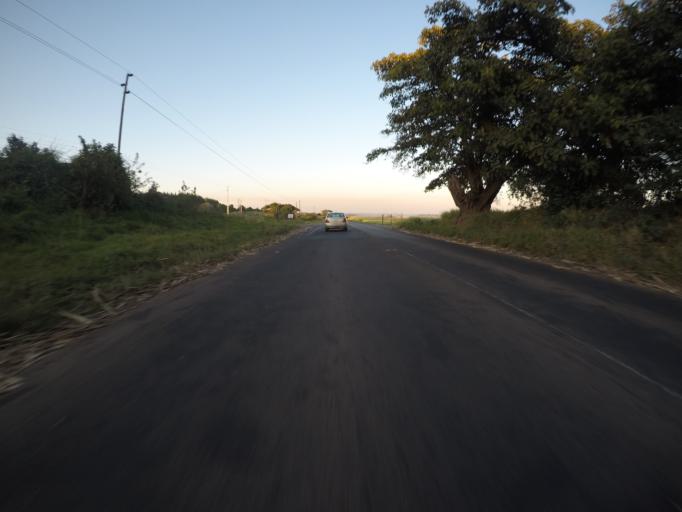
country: ZA
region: KwaZulu-Natal
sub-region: uThungulu District Municipality
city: Empangeni
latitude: -28.8041
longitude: 31.8932
